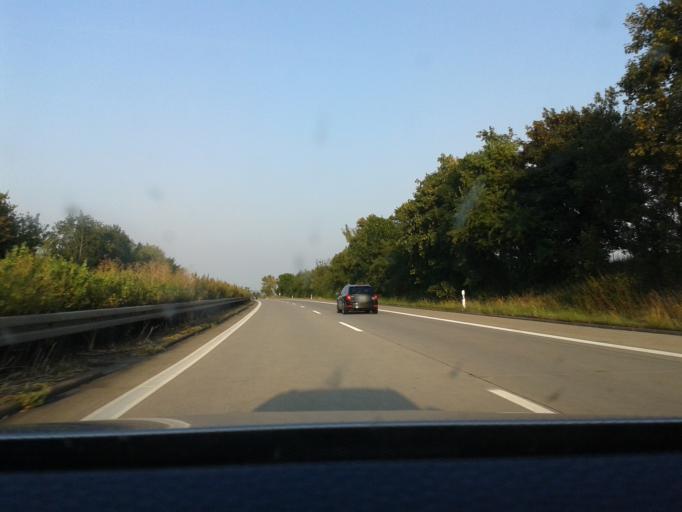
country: DE
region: Saxony
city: Grossweitzschen
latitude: 51.1676
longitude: 13.0573
